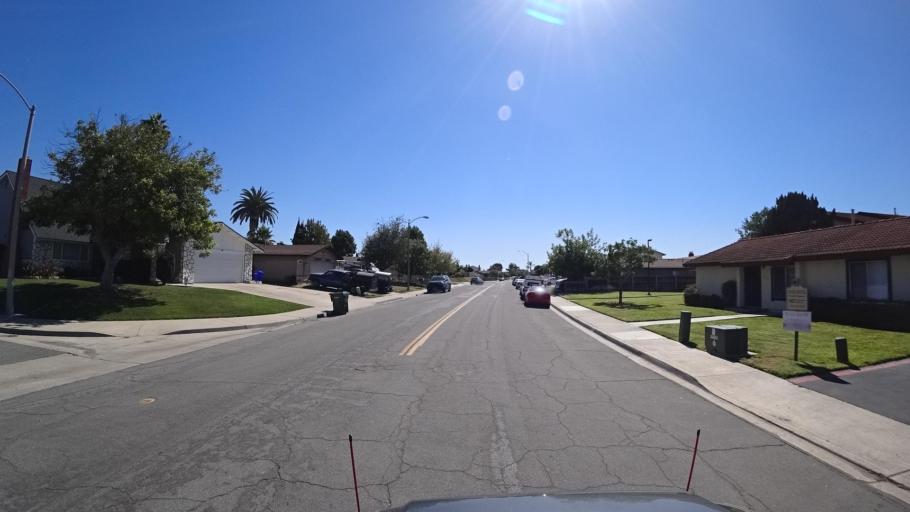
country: US
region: California
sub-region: San Diego County
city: La Presa
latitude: 32.6951
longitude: -117.0216
